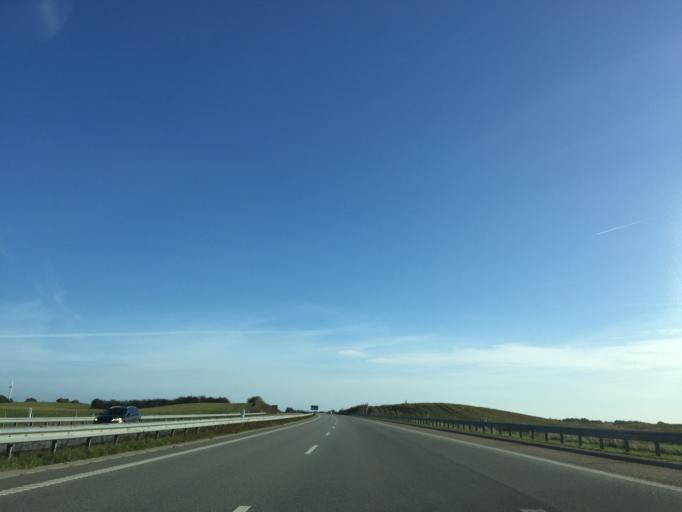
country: DK
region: South Denmark
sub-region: Aabenraa Kommune
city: Aabenraa
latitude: 54.9449
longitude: 9.4594
